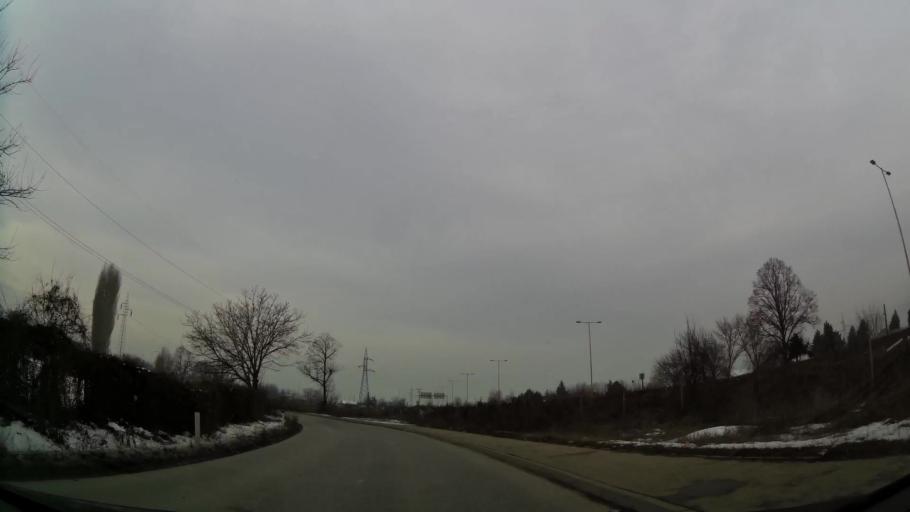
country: MK
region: Butel
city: Butel
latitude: 42.0412
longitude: 21.4516
